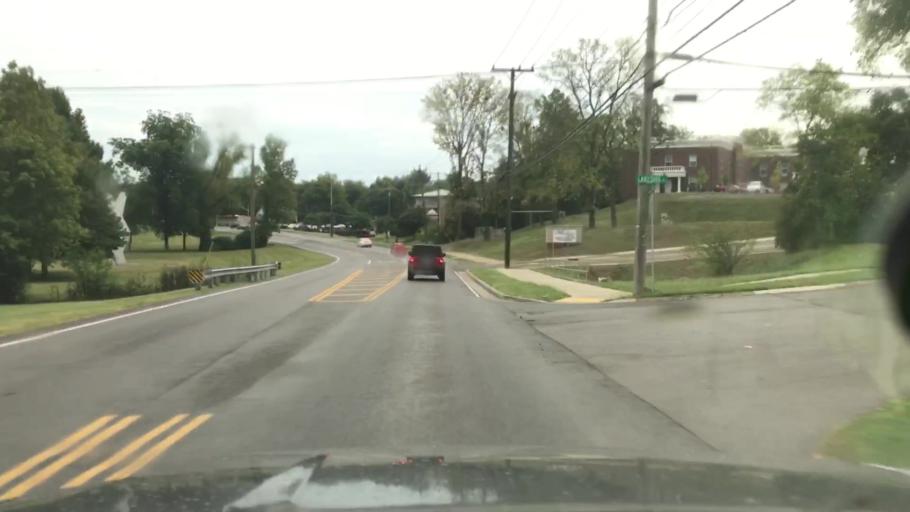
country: US
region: Tennessee
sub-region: Davidson County
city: Lakewood
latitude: 36.1764
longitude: -86.6160
